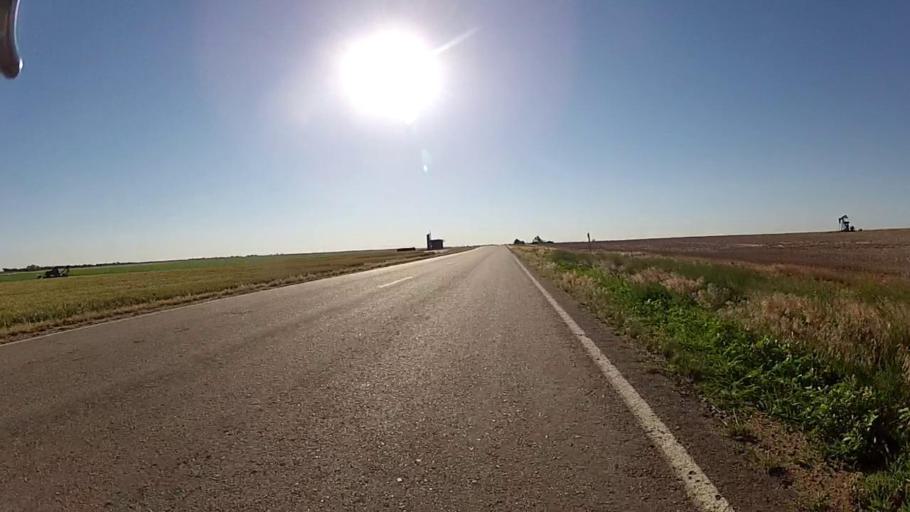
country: US
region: Kansas
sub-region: Ford County
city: Dodge City
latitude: 37.6460
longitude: -99.8227
